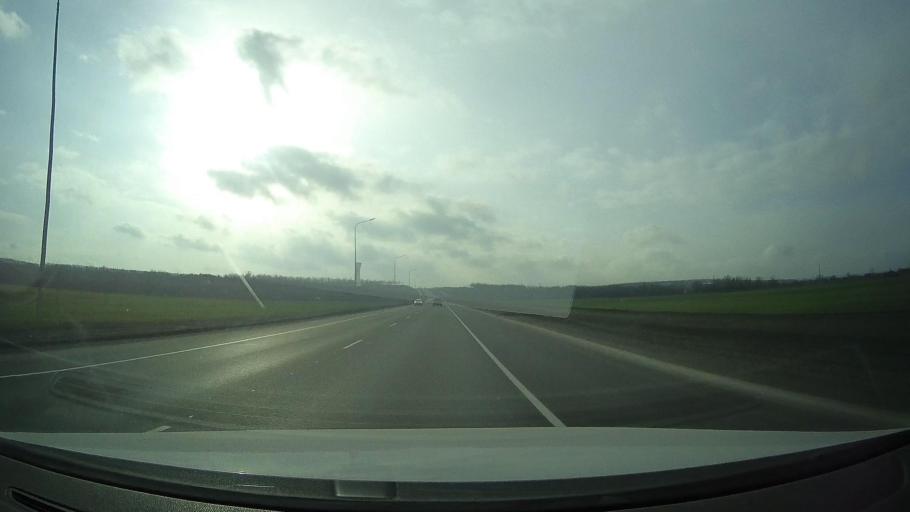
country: RU
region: Rostov
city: Grushevskaya
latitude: 47.4413
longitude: 39.8743
